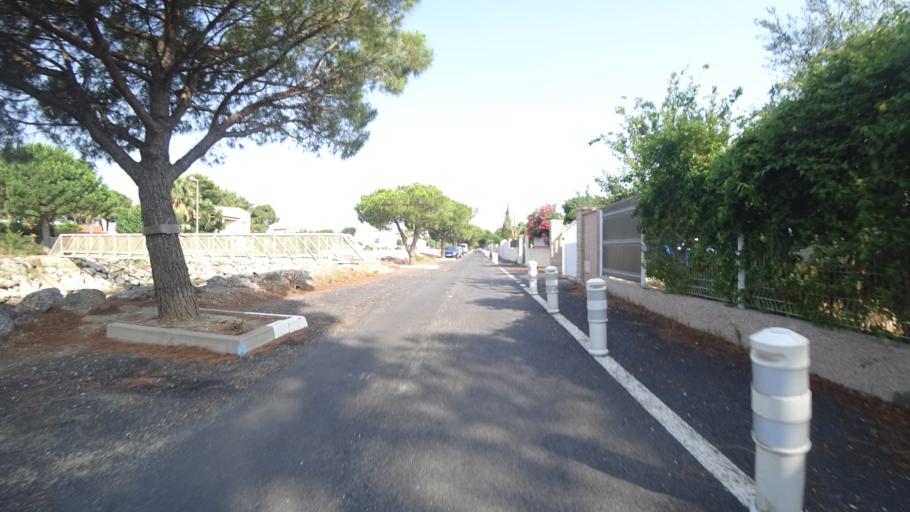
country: FR
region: Languedoc-Roussillon
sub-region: Departement des Pyrenees-Orientales
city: Sainte-Marie-Plage
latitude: 42.7258
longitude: 3.0325
